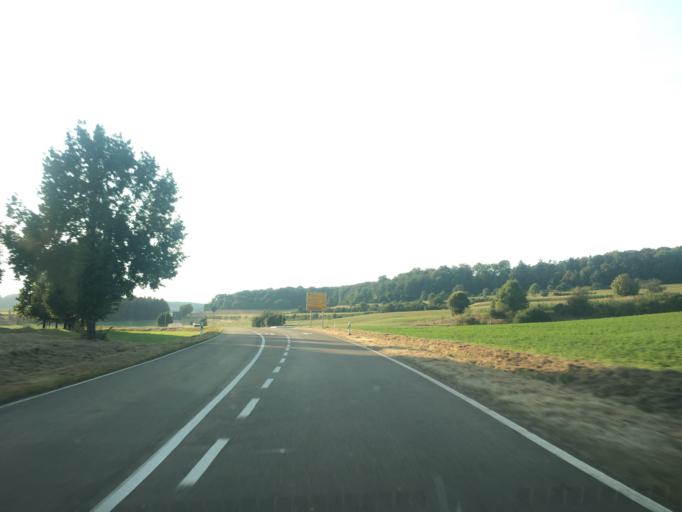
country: DE
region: Baden-Wuerttemberg
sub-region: Tuebingen Region
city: Rechtenstein
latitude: 48.2518
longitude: 9.5348
